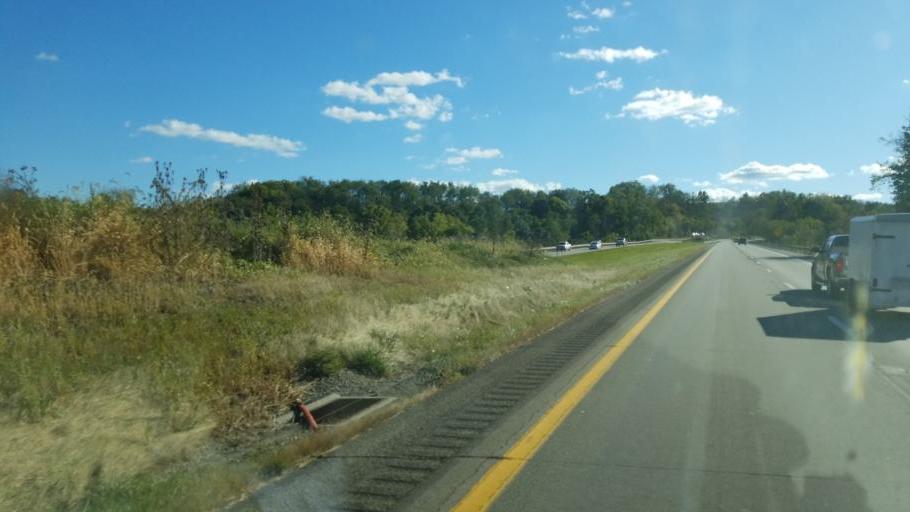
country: US
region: West Virginia
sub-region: Brooke County
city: Bethany
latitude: 40.1114
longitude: -80.4903
